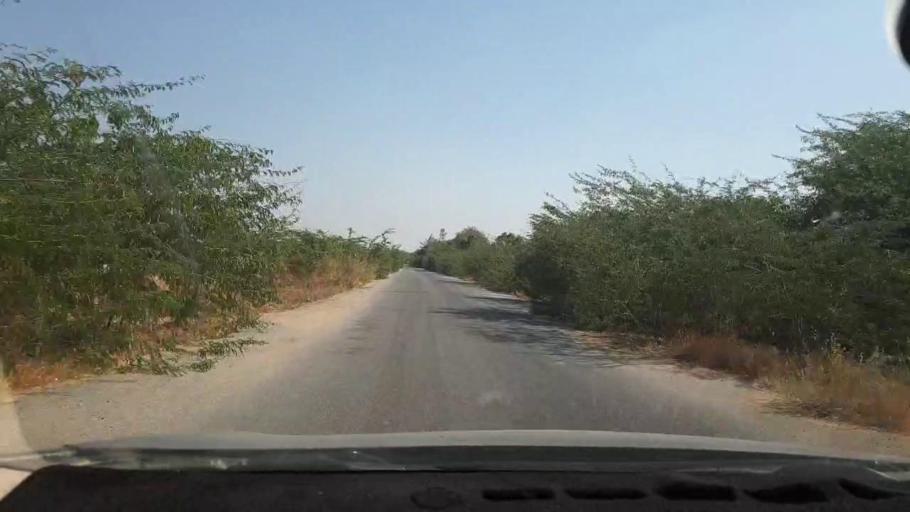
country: PK
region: Sindh
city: Malir Cantonment
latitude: 25.1419
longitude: 67.1965
